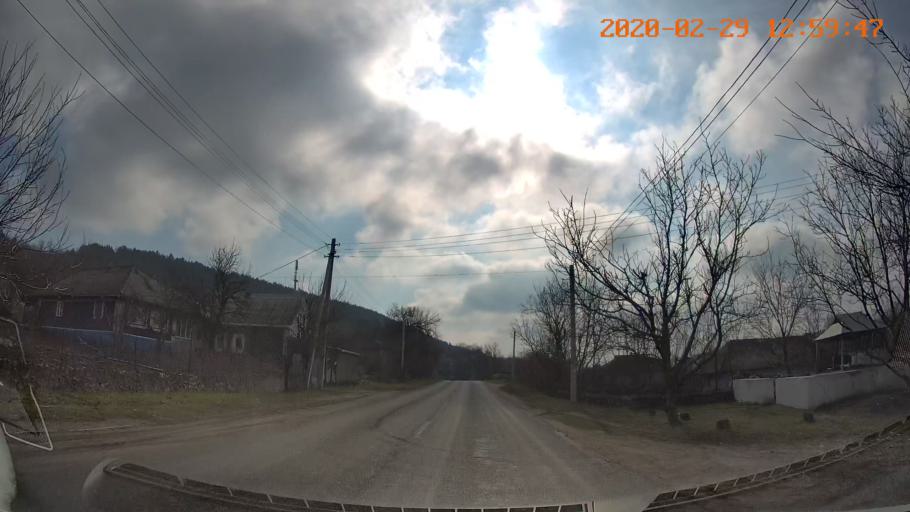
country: MD
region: Telenesti
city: Camenca
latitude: 48.0585
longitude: 28.7249
